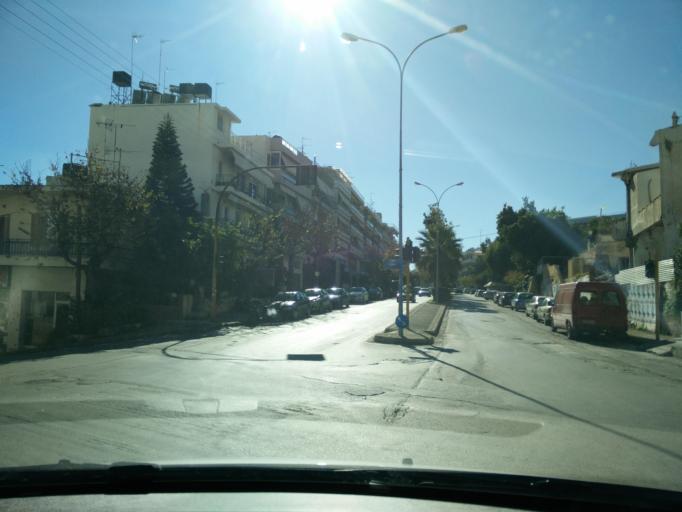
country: GR
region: Crete
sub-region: Nomos Irakleiou
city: Irakleion
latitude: 35.3315
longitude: 25.1396
